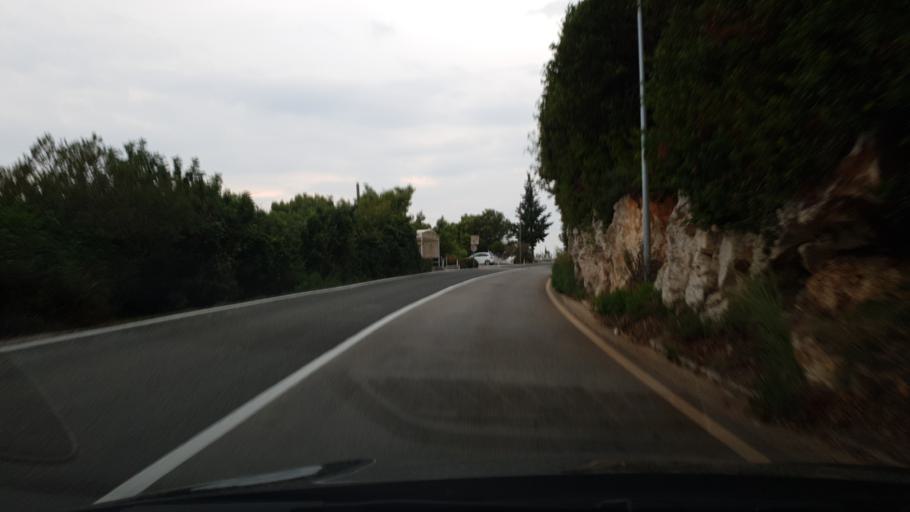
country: HR
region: Dubrovacko-Neretvanska
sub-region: Grad Dubrovnik
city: Mokosica
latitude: 42.6732
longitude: 18.0670
